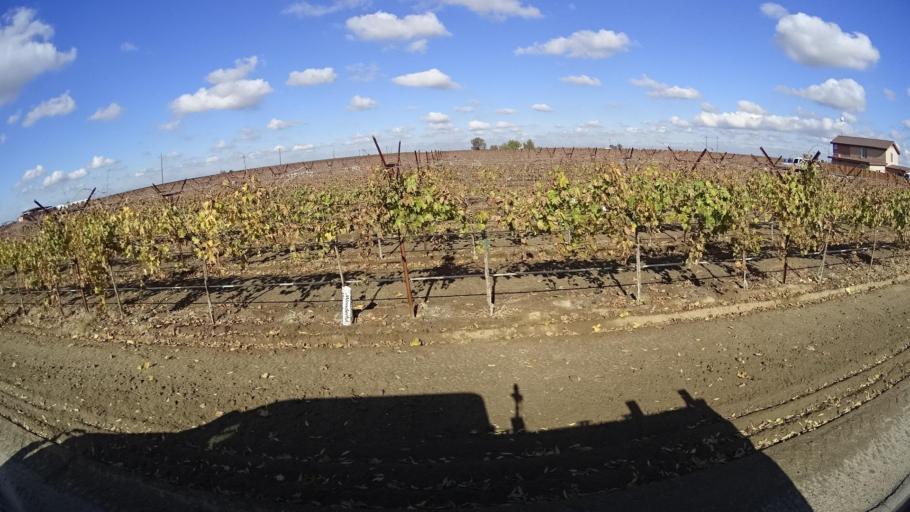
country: US
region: California
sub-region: Kern County
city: Delano
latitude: 35.7322
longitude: -119.3470
